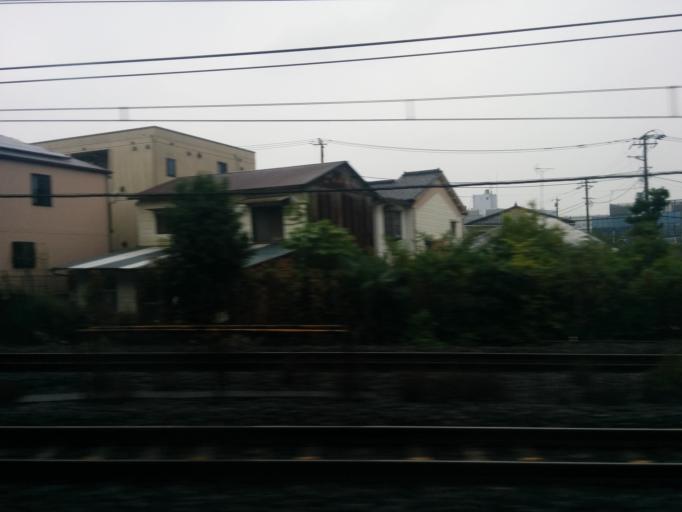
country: JP
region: Chiba
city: Funabashi
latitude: 35.7021
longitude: 139.9758
